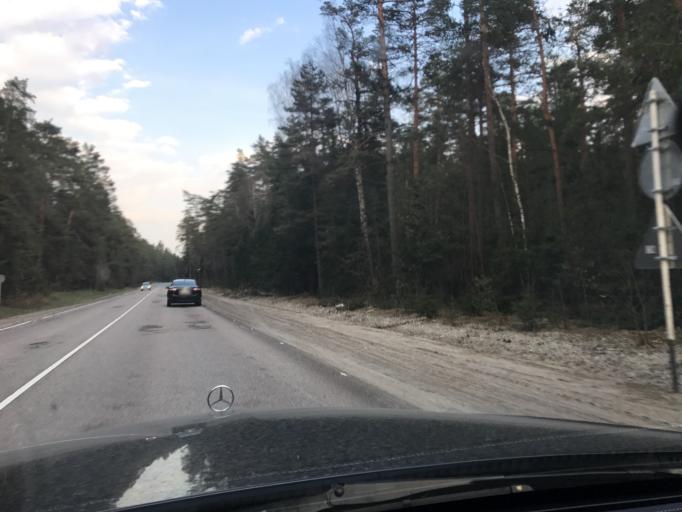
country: RU
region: Vladimir
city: Muromtsevo
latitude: 55.9581
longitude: 40.9801
